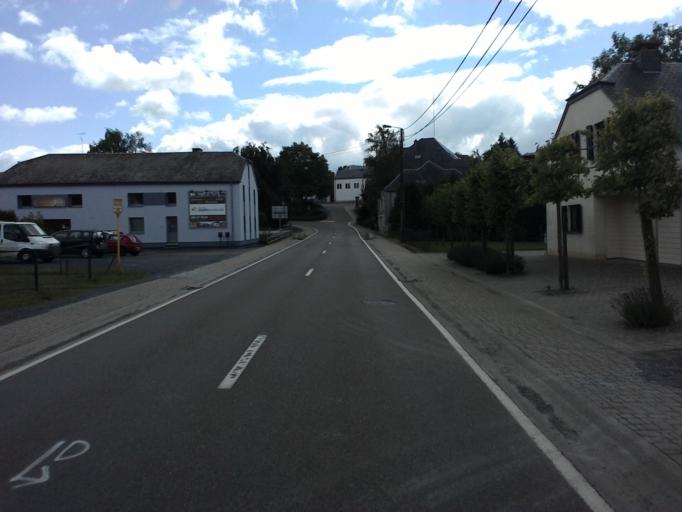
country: BE
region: Wallonia
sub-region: Province du Luxembourg
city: Leglise
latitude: 49.7998
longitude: 5.5347
